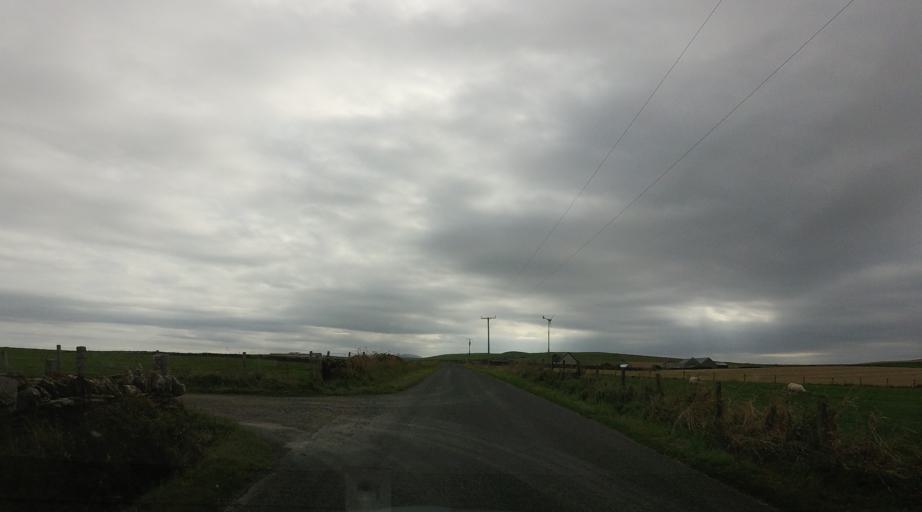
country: GB
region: Scotland
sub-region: Orkney Islands
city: Stromness
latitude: 59.0358
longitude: -3.3121
